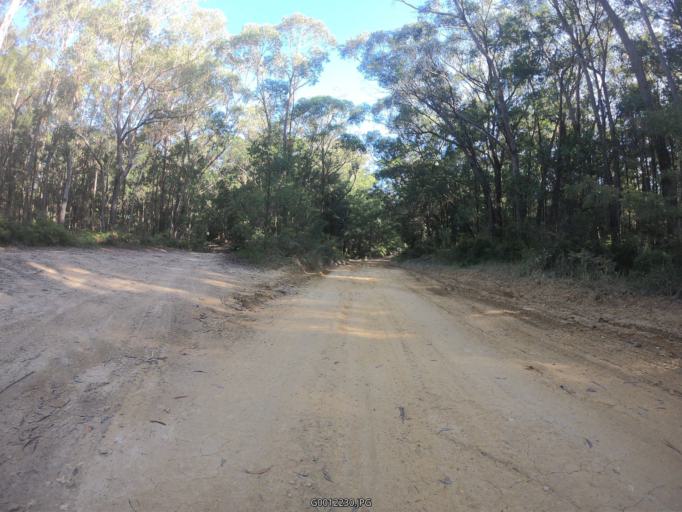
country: AU
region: New South Wales
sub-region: Lake Macquarie Shire
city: Cooranbong
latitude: -33.0845
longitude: 151.3572
